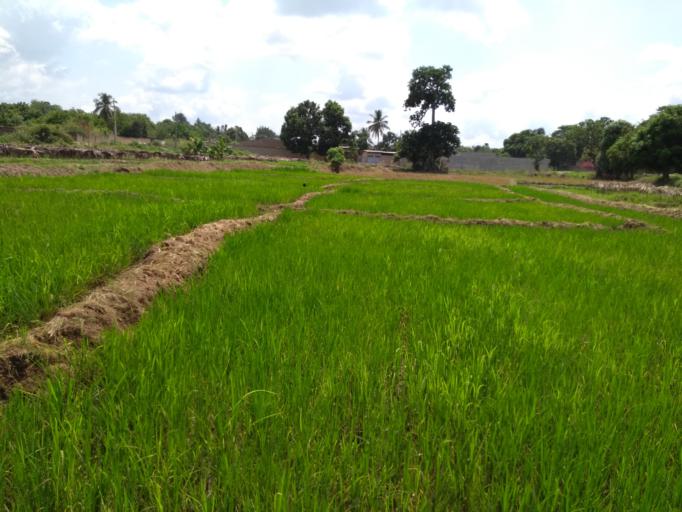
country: CI
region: Vallee du Bandama
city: Bouake
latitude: 7.6899
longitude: -5.0044
